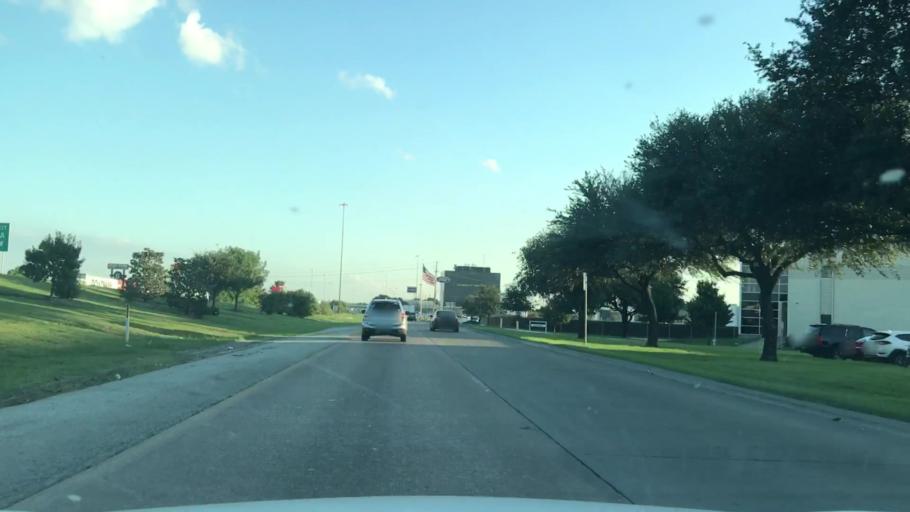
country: US
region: Texas
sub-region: Dallas County
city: Mesquite
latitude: 32.8087
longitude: -96.6281
